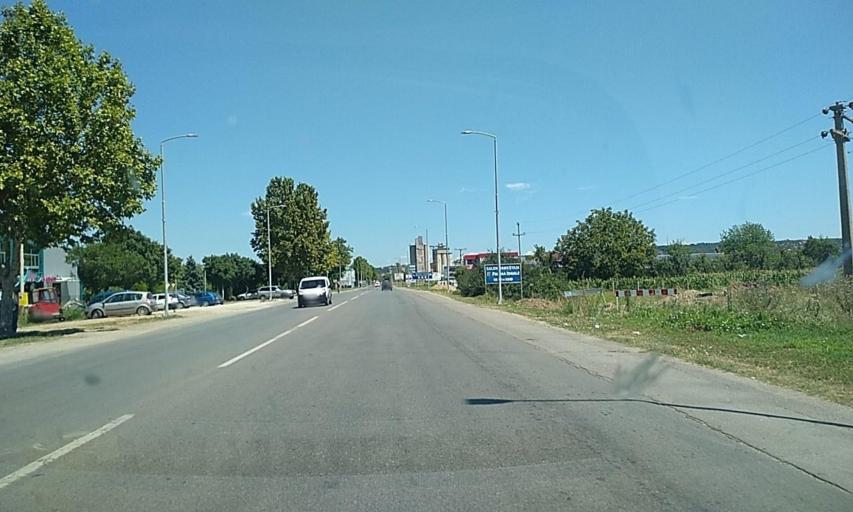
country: RS
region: Central Serbia
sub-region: Branicevski Okrug
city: Pozarevac
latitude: 44.6044
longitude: 21.1635
